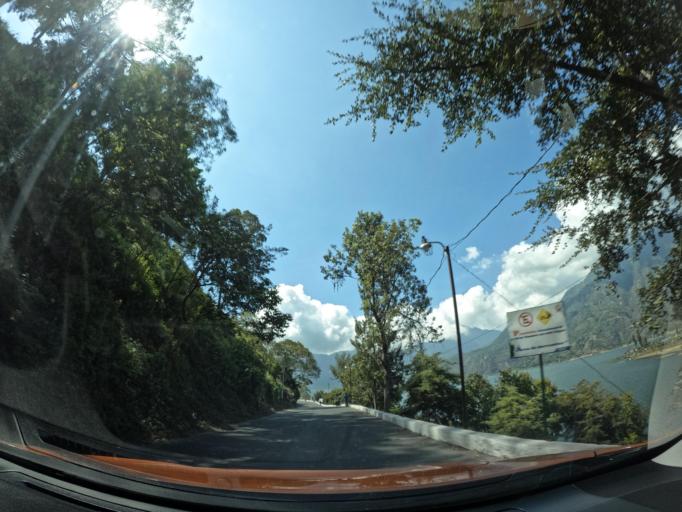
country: GT
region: Solola
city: Santiago Atitlan
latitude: 14.6331
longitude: -91.2311
